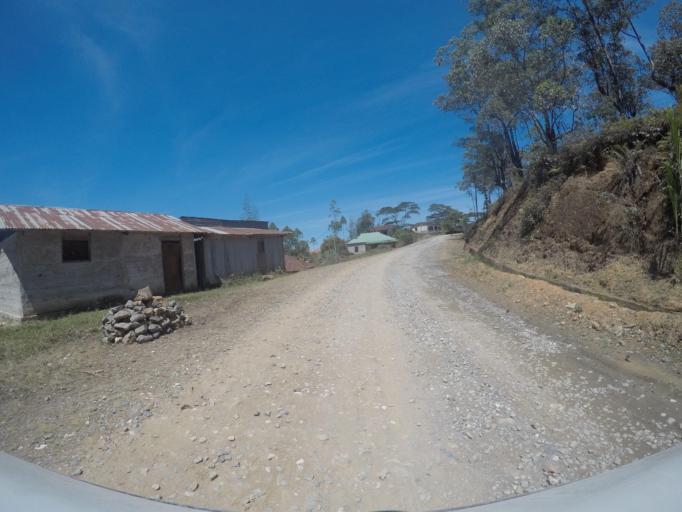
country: TL
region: Ermera
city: Gleno
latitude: -8.7855
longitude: 125.3763
